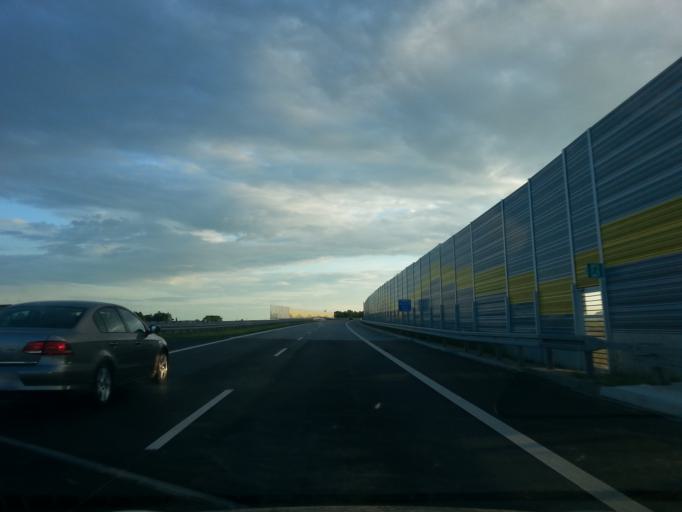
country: PL
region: Lodz Voivodeship
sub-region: Powiat wieruszowski
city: Lututow
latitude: 51.3217
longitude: 18.4344
